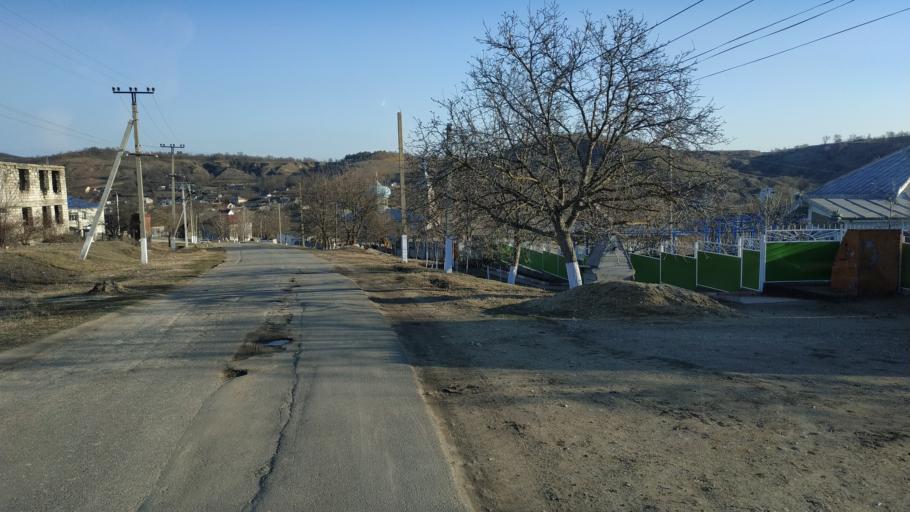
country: MD
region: Hincesti
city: Hincesti
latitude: 46.7009
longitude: 28.5423
